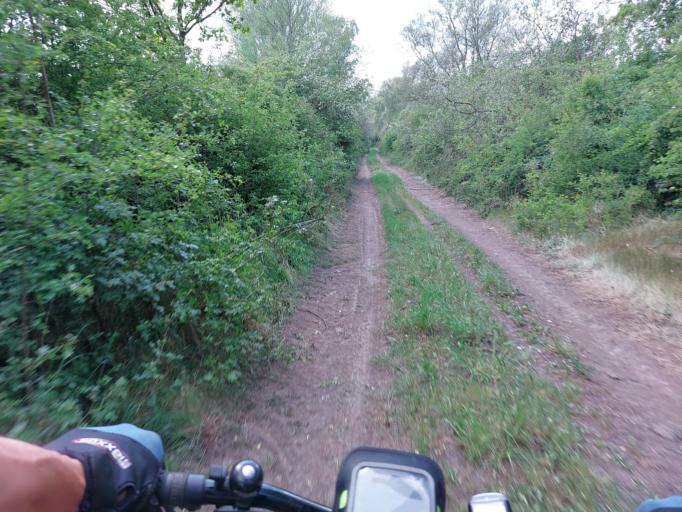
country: BE
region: Wallonia
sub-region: Province du Hainaut
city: Quaregnon
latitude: 50.4592
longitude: 3.8543
